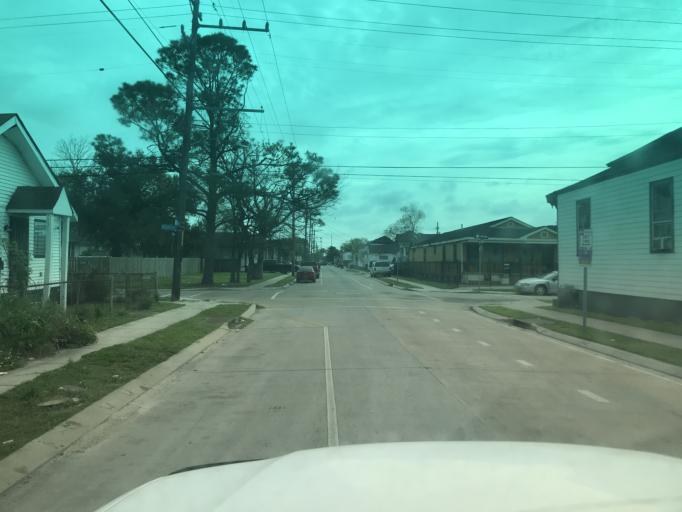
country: US
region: Louisiana
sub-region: Orleans Parish
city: New Orleans
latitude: 29.9788
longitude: -90.0555
